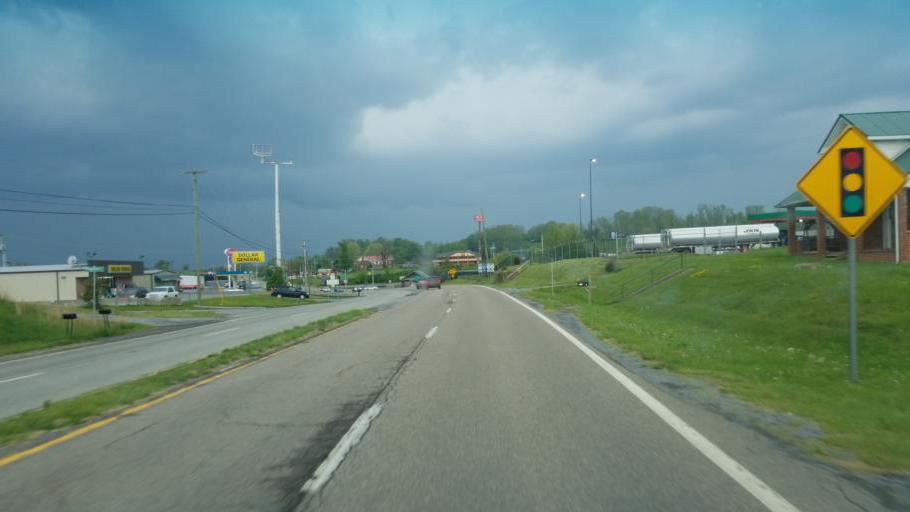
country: US
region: Virginia
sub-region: Washington County
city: Glade Spring
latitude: 36.7698
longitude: -81.7777
